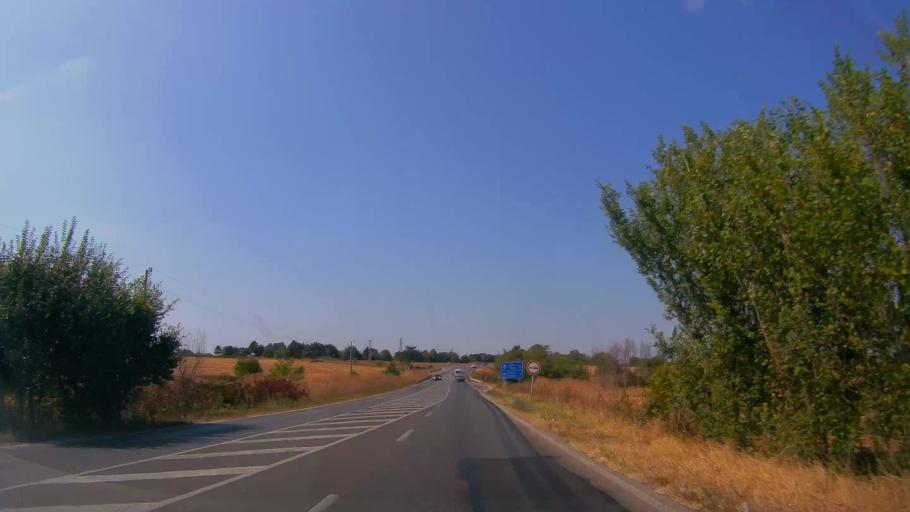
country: BG
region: Razgrad
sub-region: Obshtina Tsar Kaloyan
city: Tsar Kaloyan
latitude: 43.5671
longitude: 26.3272
